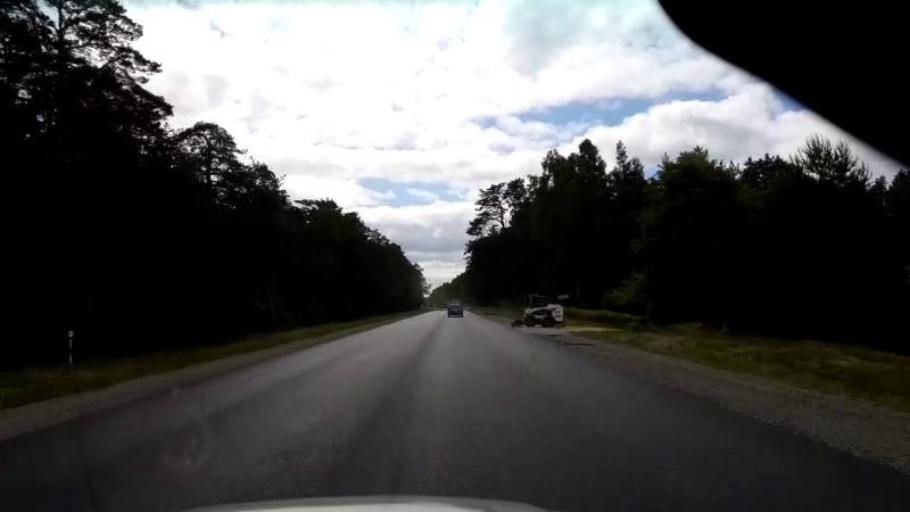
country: LV
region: Salacgrivas
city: Ainazi
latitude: 57.8263
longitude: 24.3449
